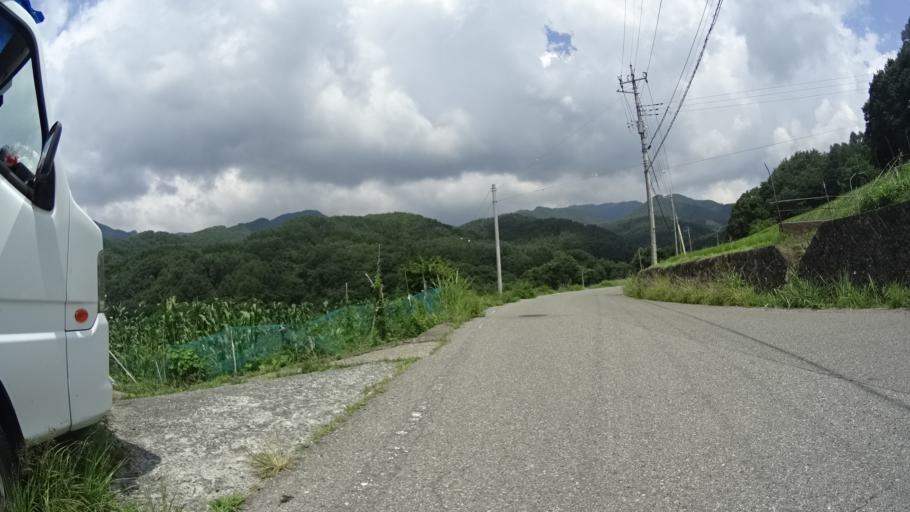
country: JP
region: Yamanashi
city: Nirasaki
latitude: 35.8797
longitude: 138.5199
